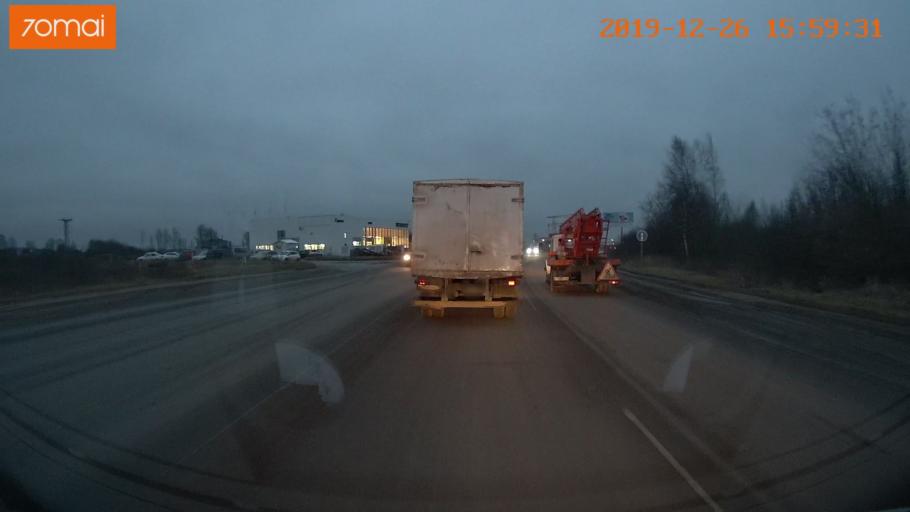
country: RU
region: Jaroslavl
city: Rybinsk
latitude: 58.0310
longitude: 38.8044
